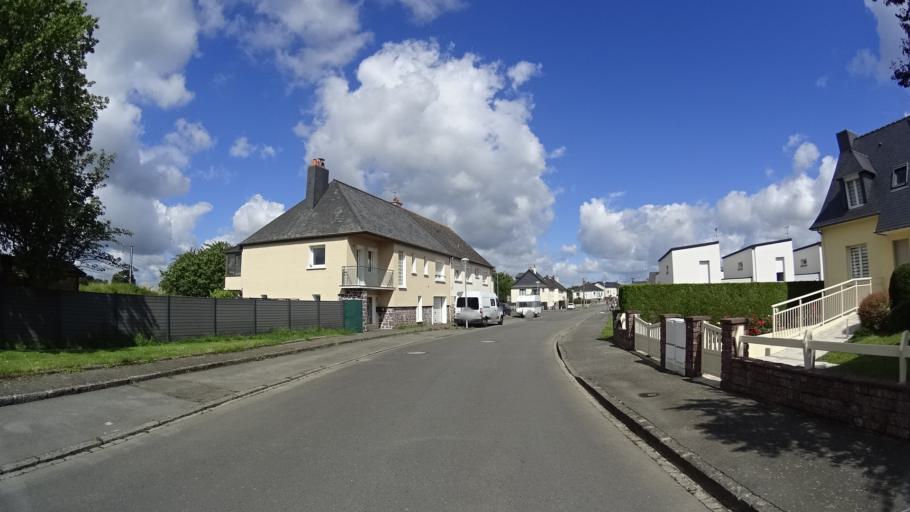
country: FR
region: Brittany
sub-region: Departement d'Ille-et-Vilaine
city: Le Rheu
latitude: 48.1225
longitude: -1.8084
